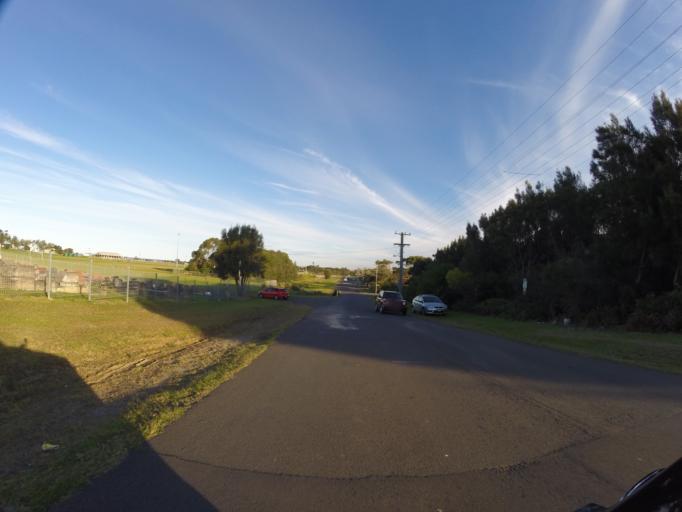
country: AU
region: New South Wales
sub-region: Wollongong
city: Bulli
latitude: -34.3420
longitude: 150.9201
